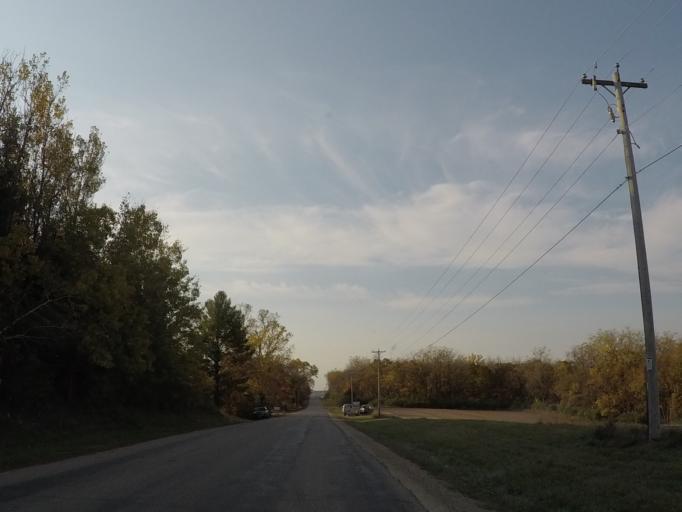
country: US
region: Wisconsin
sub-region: Dane County
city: Cross Plains
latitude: 43.0471
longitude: -89.6012
